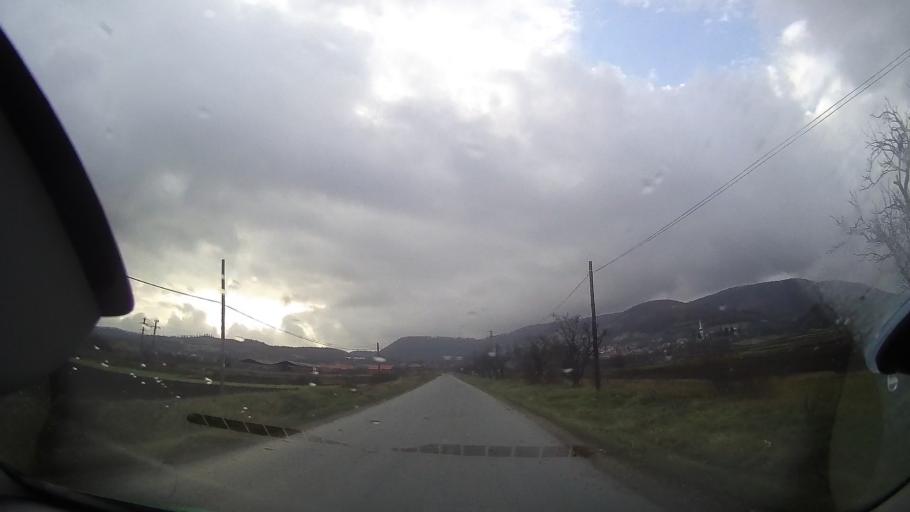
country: RO
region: Cluj
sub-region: Comuna Moldovenesti
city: Moldovenesti
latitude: 46.5060
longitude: 23.6679
